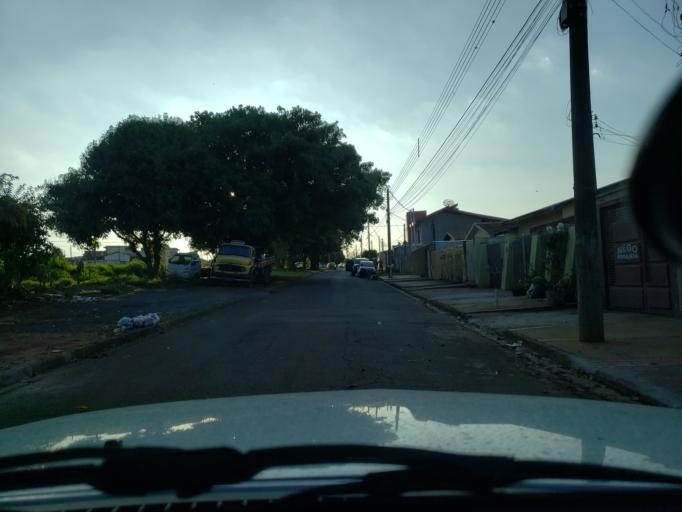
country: BR
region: Sao Paulo
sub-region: Moji-Guacu
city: Mogi-Gaucu
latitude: -22.3422
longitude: -46.9379
